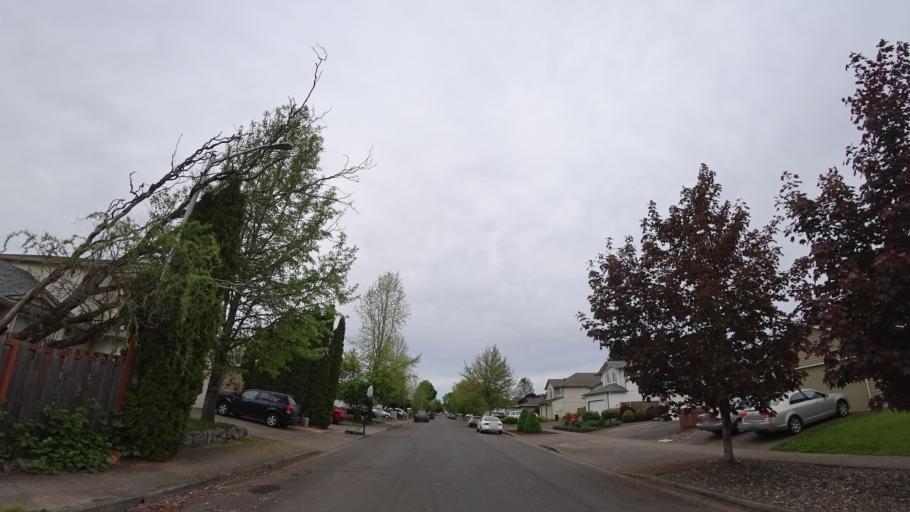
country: US
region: Oregon
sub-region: Washington County
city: Aloha
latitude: 45.5142
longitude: -122.9101
